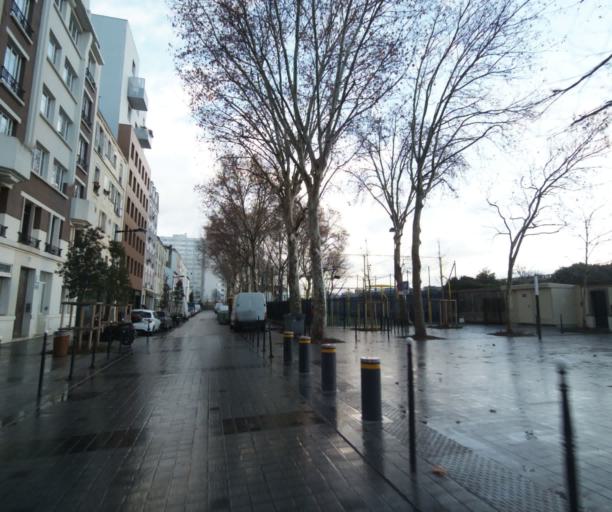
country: FR
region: Ile-de-France
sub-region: Departement des Hauts-de-Seine
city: Clichy
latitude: 48.8972
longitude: 2.3036
